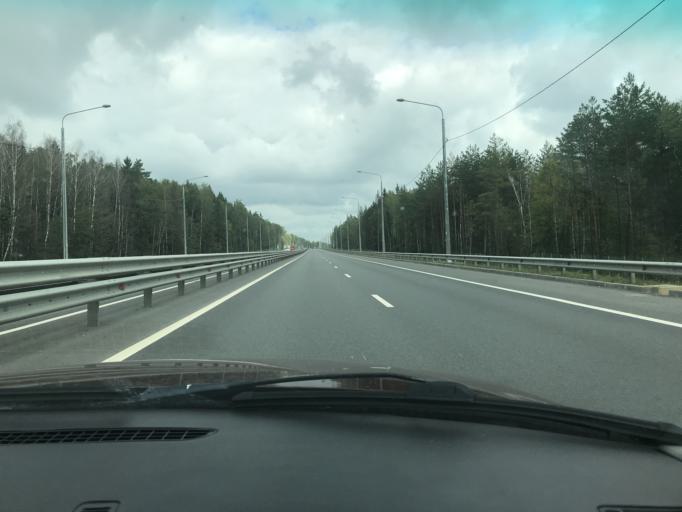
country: RU
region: Kaluga
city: Pyatovskiy
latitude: 54.7142
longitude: 36.1650
